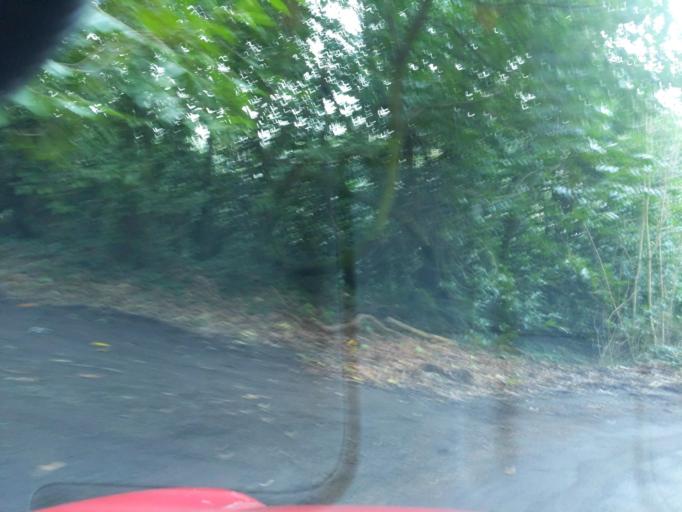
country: GB
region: England
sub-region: Devon
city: Wembury
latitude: 50.3272
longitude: -4.0800
